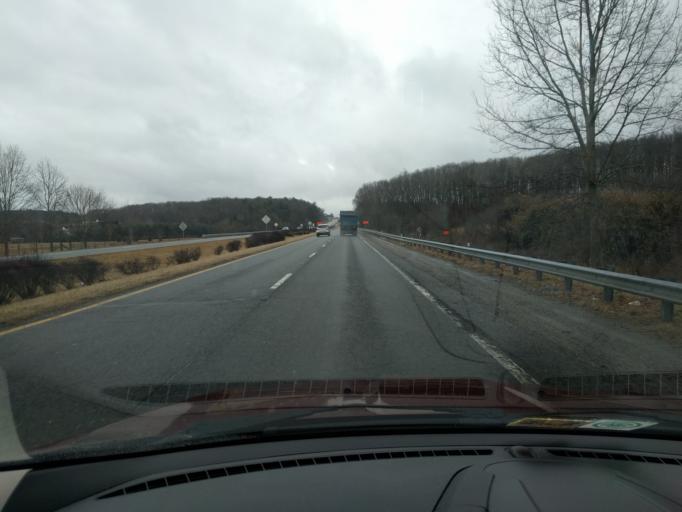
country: US
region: Virginia
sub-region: Montgomery County
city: Merrimac
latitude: 37.2048
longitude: -80.4204
